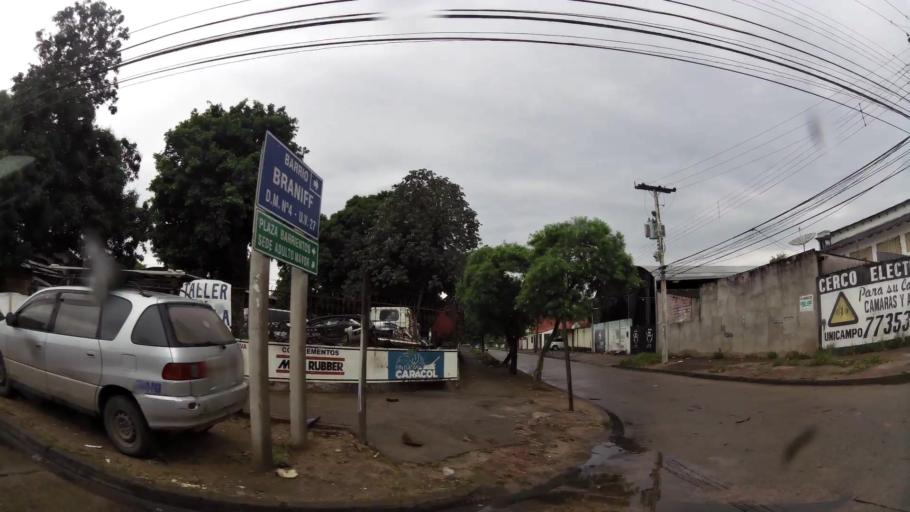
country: BO
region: Santa Cruz
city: Santa Cruz de la Sierra
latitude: -17.8086
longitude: -63.1873
